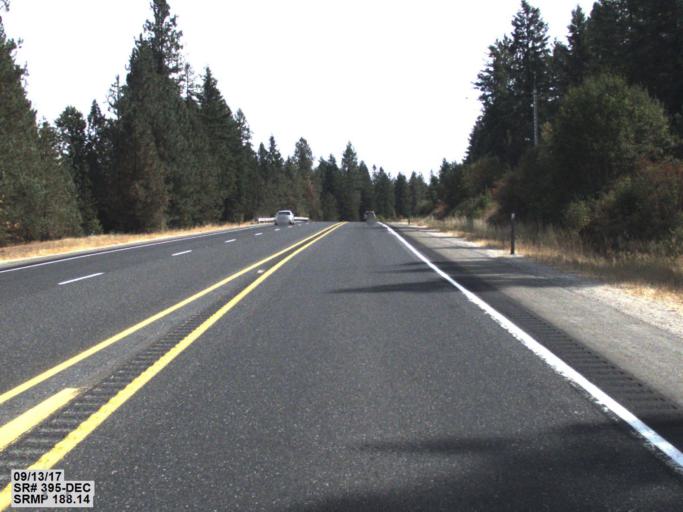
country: US
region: Washington
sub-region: Spokane County
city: Deer Park
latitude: 48.0289
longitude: -117.5988
